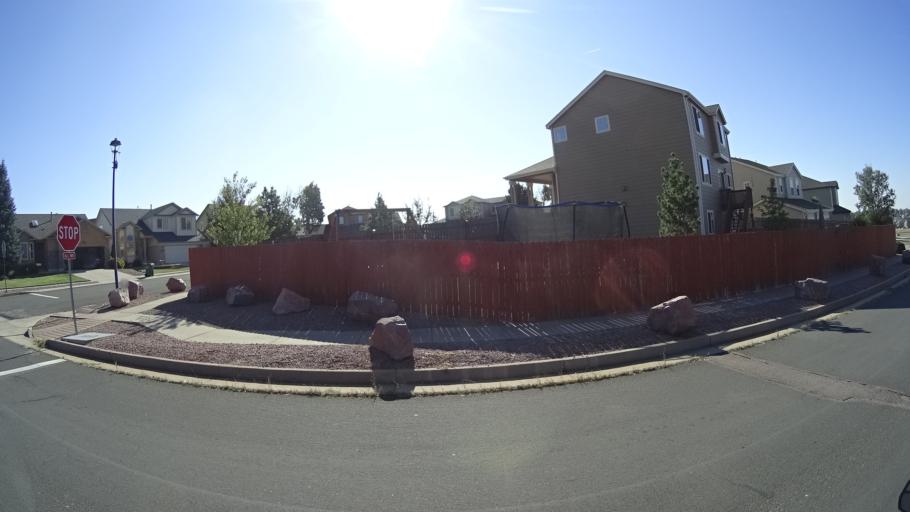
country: US
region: Colorado
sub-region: El Paso County
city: Cimarron Hills
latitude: 38.8889
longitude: -104.7010
